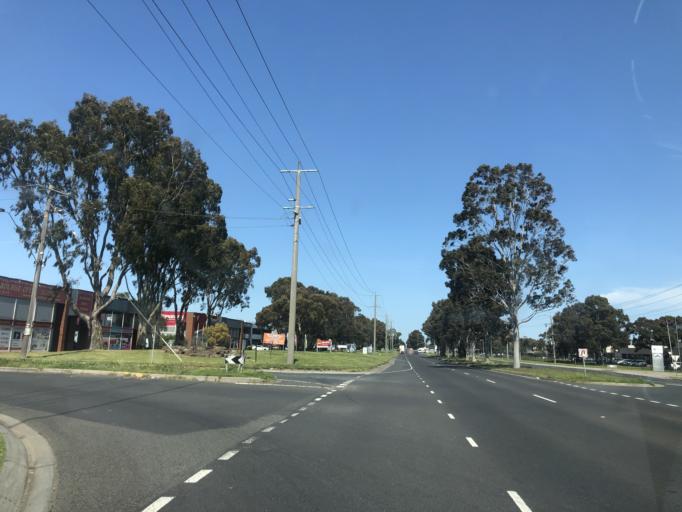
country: AU
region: Victoria
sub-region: Casey
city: Hampton Park
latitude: -38.0285
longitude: 145.2127
